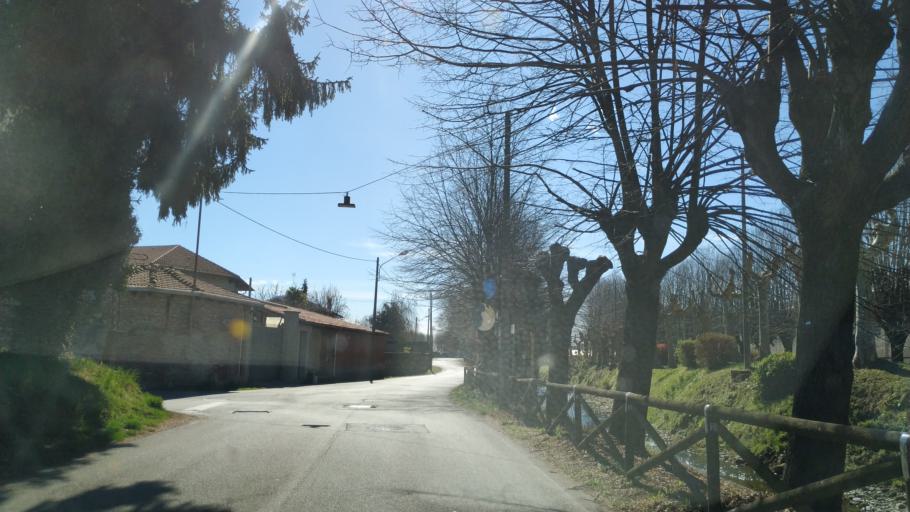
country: IT
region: Piedmont
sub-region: Provincia di Novara
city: Ghemme
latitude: 45.5942
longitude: 8.4216
